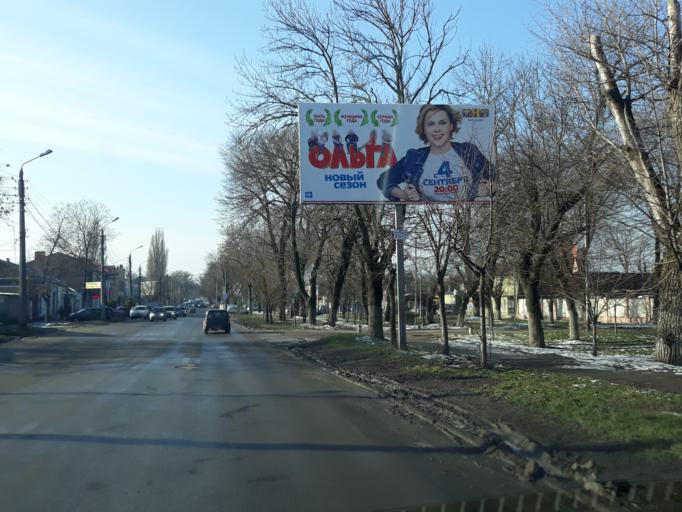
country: RU
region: Rostov
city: Taganrog
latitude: 47.2156
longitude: 38.9128
